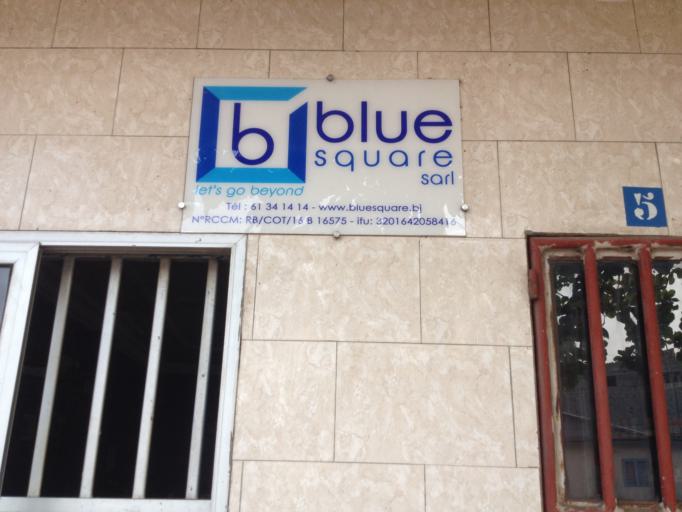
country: BJ
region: Littoral
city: Cotonou
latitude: 6.3799
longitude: 2.4391
